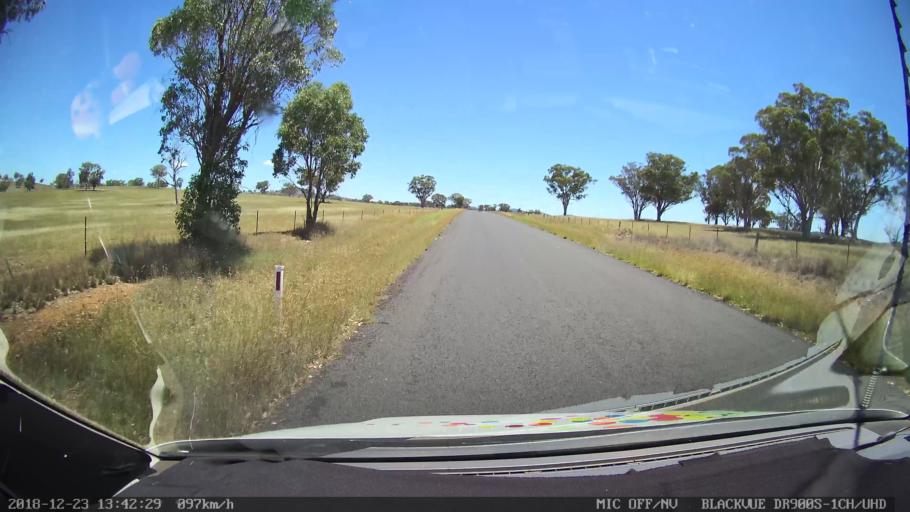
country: AU
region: New South Wales
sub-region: Armidale Dumaresq
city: Armidale
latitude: -30.4775
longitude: 151.1622
